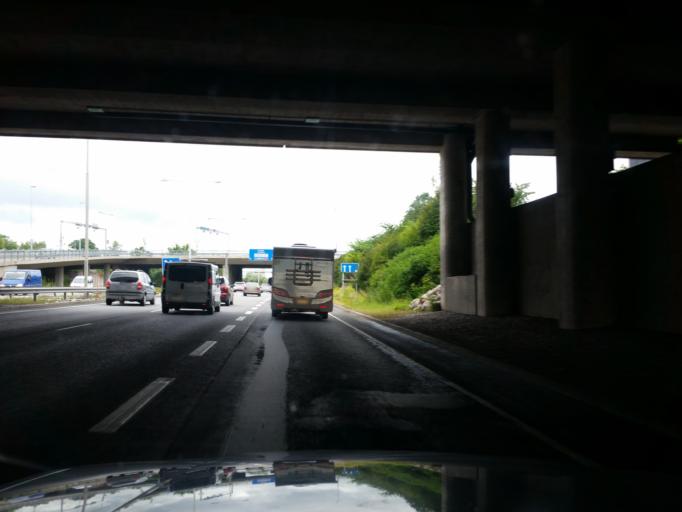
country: FI
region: Varsinais-Suomi
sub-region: Turku
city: Turku
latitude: 60.4534
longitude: 22.2940
